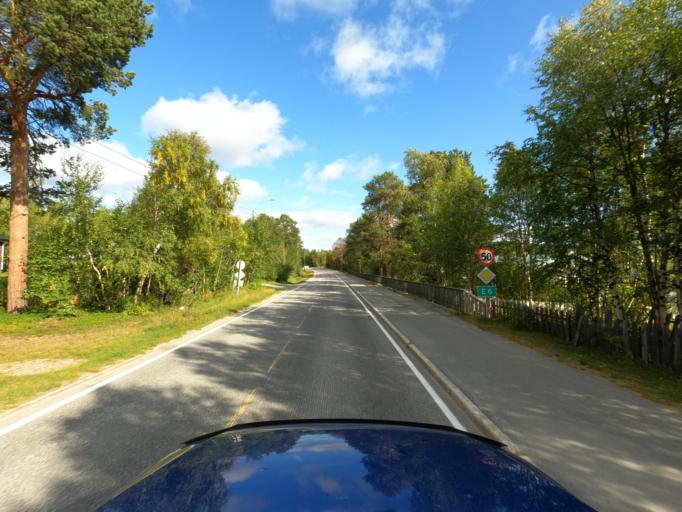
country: NO
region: Finnmark Fylke
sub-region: Karasjok
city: Karasjohka
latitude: 69.4751
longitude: 25.5125
